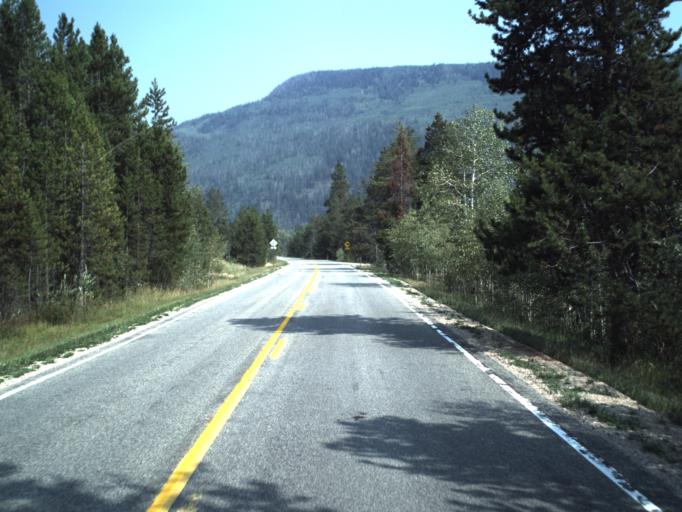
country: US
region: Utah
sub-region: Summit County
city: Francis
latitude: 40.5782
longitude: -111.0406
